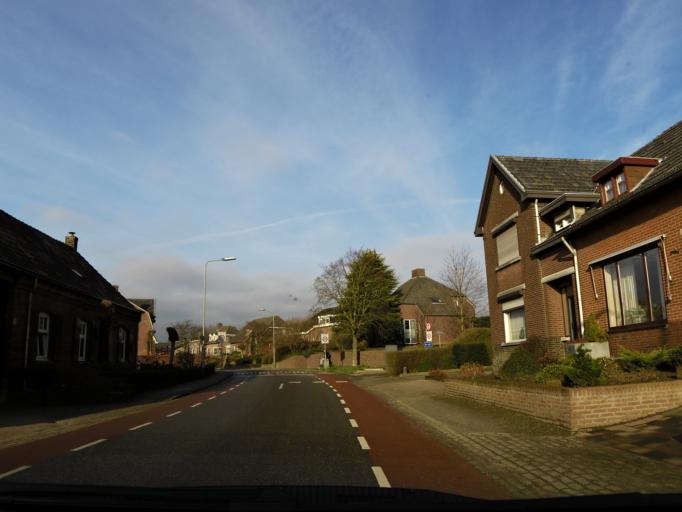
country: NL
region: Limburg
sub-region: Gemeente Beesel
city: Beesel
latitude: 51.2669
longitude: 6.0479
